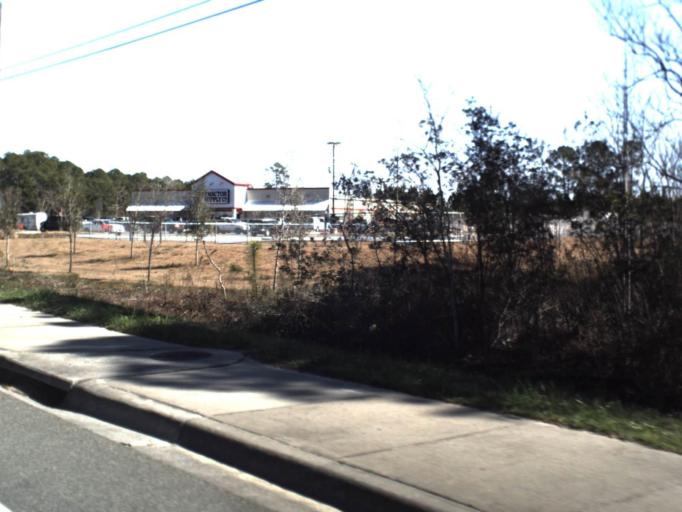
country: US
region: Florida
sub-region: Bay County
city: Lynn Haven
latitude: 30.2752
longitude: -85.6391
